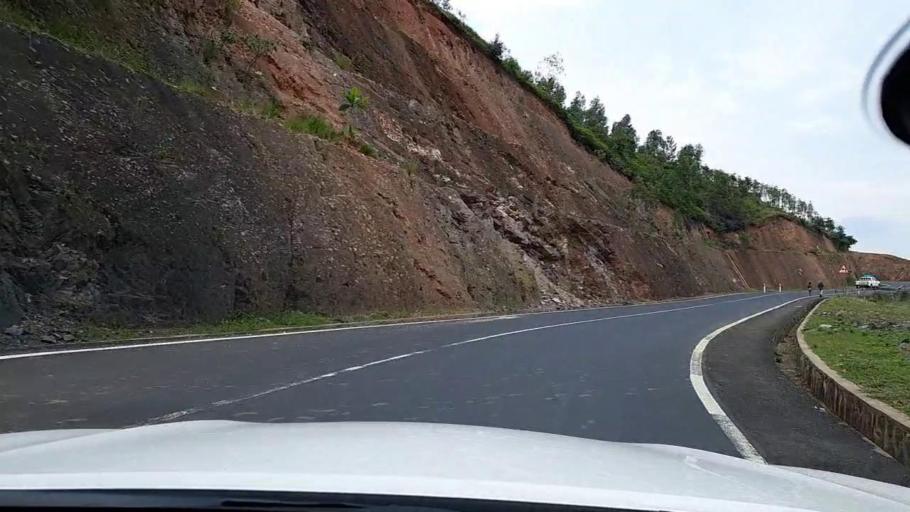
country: RW
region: Western Province
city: Kibuye
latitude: -2.1687
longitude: 29.2916
